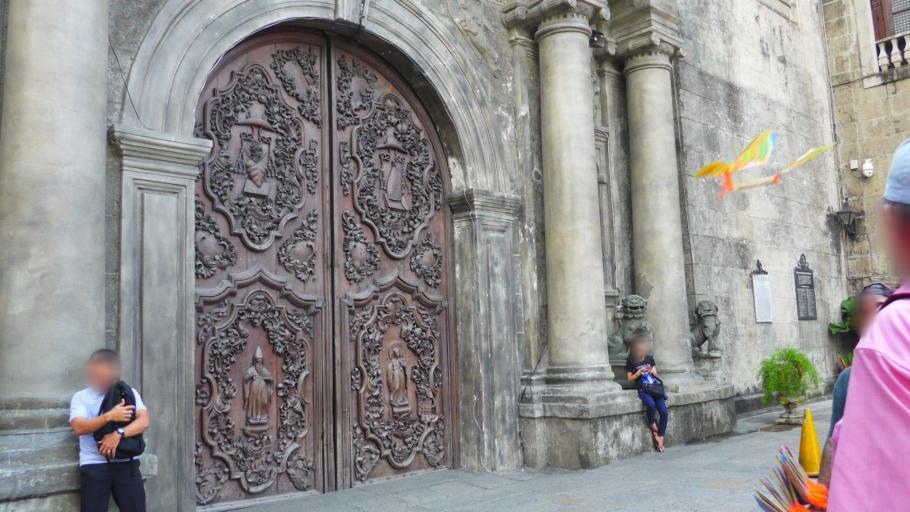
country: PH
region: Metro Manila
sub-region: City of Manila
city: Port Area
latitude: 14.5891
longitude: 120.9751
